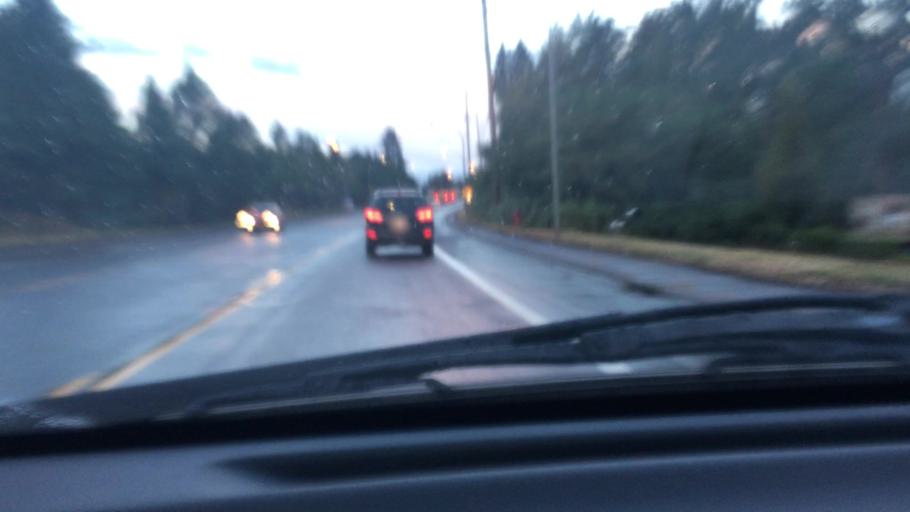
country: US
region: Oregon
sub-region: Washington County
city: King City
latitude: 45.3705
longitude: -122.7976
